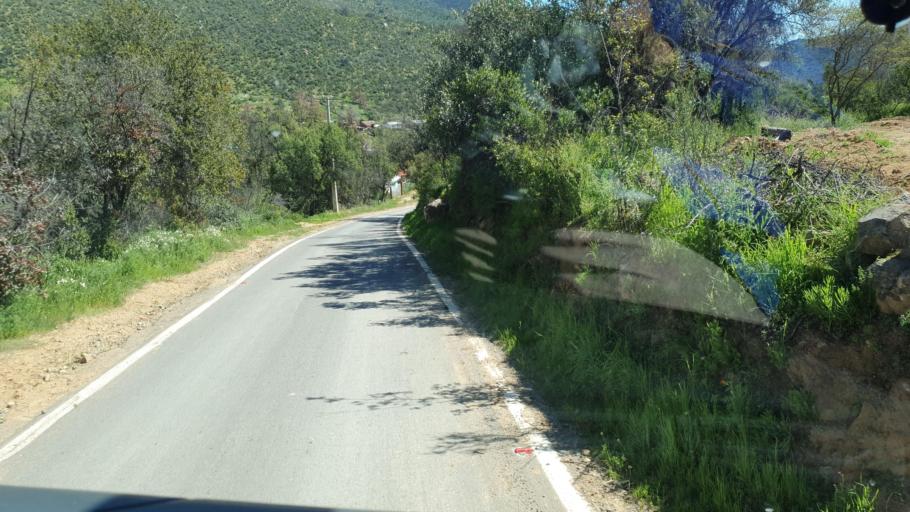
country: CL
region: Santiago Metropolitan
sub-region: Provincia de Chacabuco
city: Lampa
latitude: -33.1947
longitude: -71.0917
